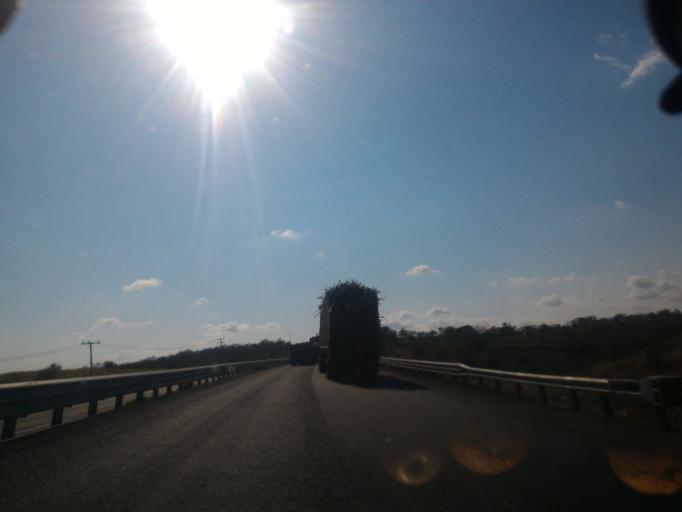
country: MX
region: Jalisco
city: Tonila
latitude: 19.4269
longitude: -103.5000
